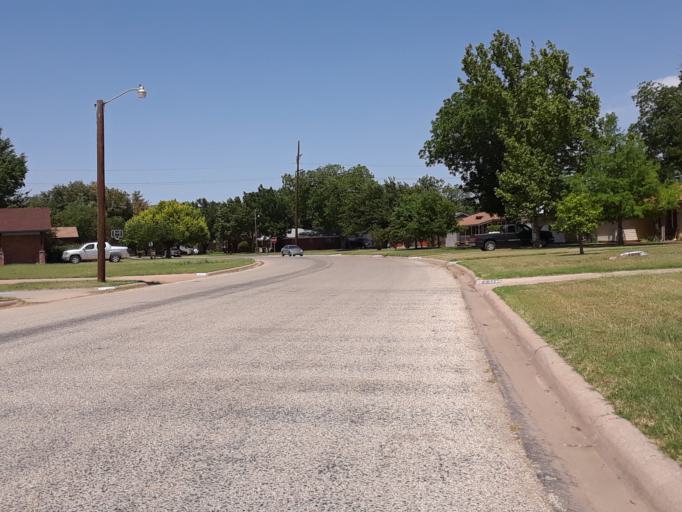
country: US
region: Texas
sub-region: Taylor County
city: Abilene
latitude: 32.4112
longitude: -99.7508
